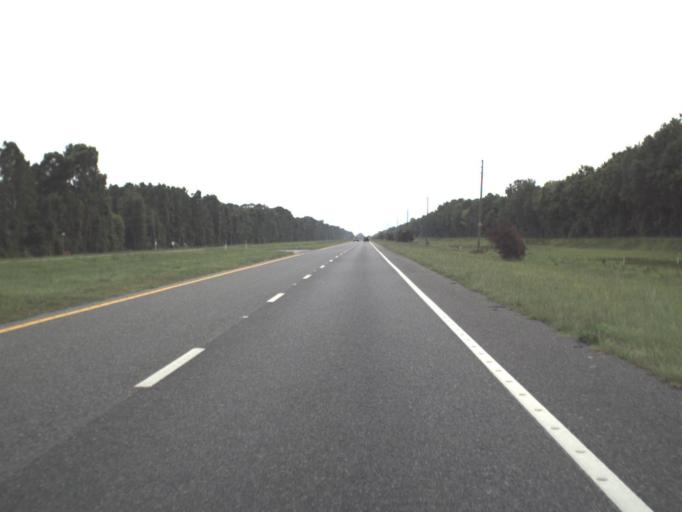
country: US
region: Florida
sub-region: Levy County
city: Inglis
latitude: 29.2157
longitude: -82.7002
